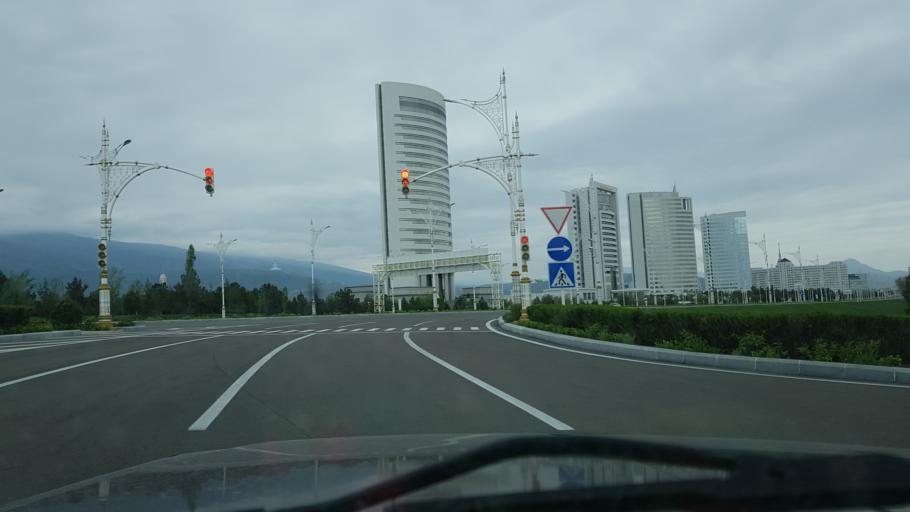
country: TM
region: Ahal
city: Ashgabat
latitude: 37.8886
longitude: 58.3515
